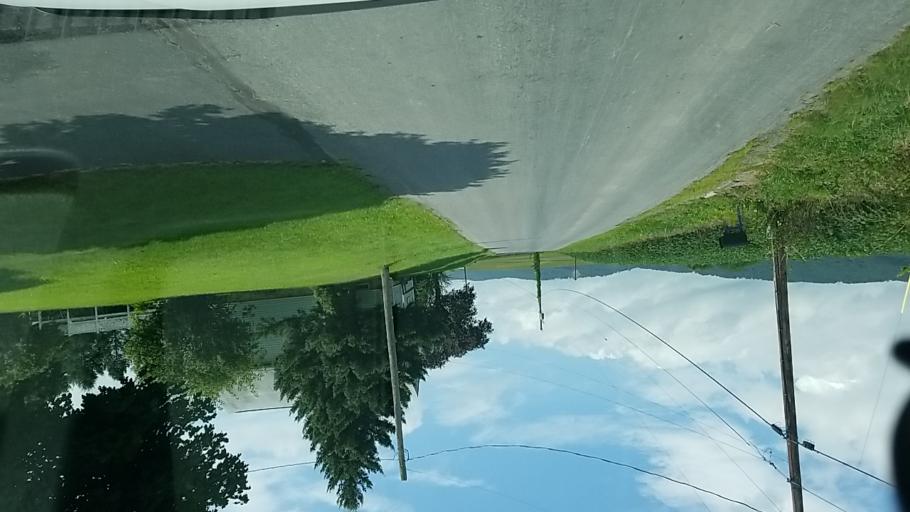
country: US
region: Pennsylvania
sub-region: Dauphin County
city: Millersburg
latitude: 40.5821
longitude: -76.8961
